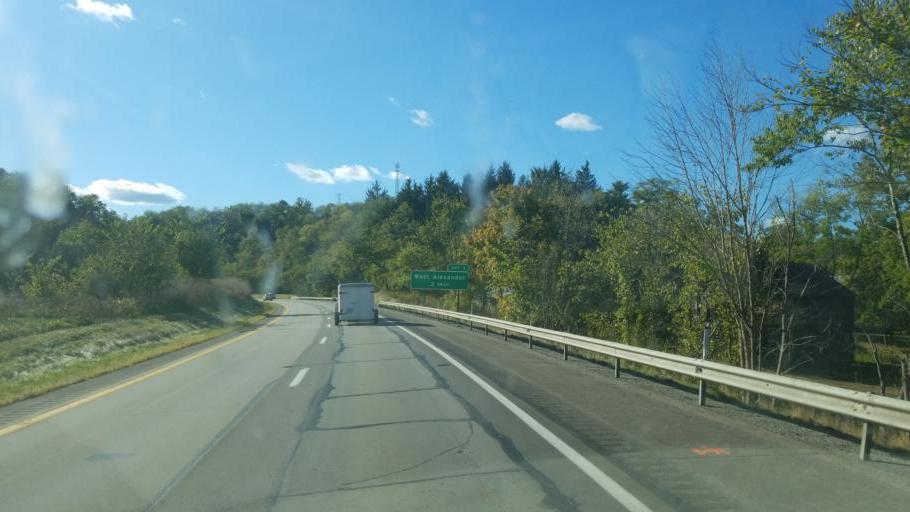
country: US
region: West Virginia
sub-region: Brooke County
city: Bethany
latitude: 40.1192
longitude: -80.4734
